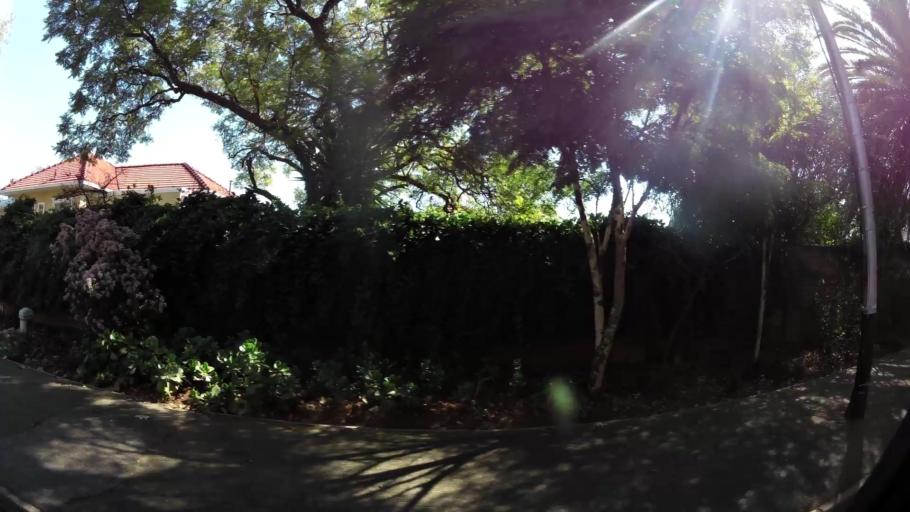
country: ZA
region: Gauteng
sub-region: City of Johannesburg Metropolitan Municipality
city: Johannesburg
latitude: -26.1691
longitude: 28.0214
